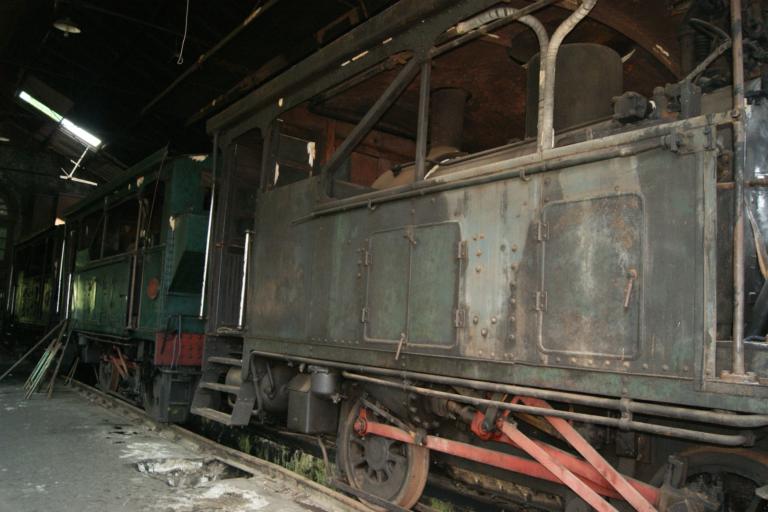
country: BR
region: Sao Paulo
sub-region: Rio Grande Da Serra
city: Rio Grande da Serra
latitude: -23.7792
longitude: -46.3029
